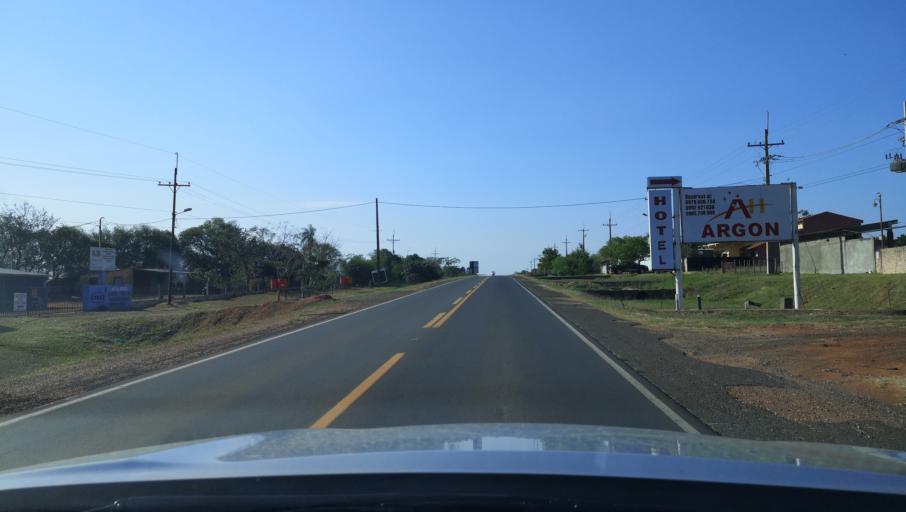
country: PY
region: Misiones
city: Santa Maria
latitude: -26.8562
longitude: -57.0353
